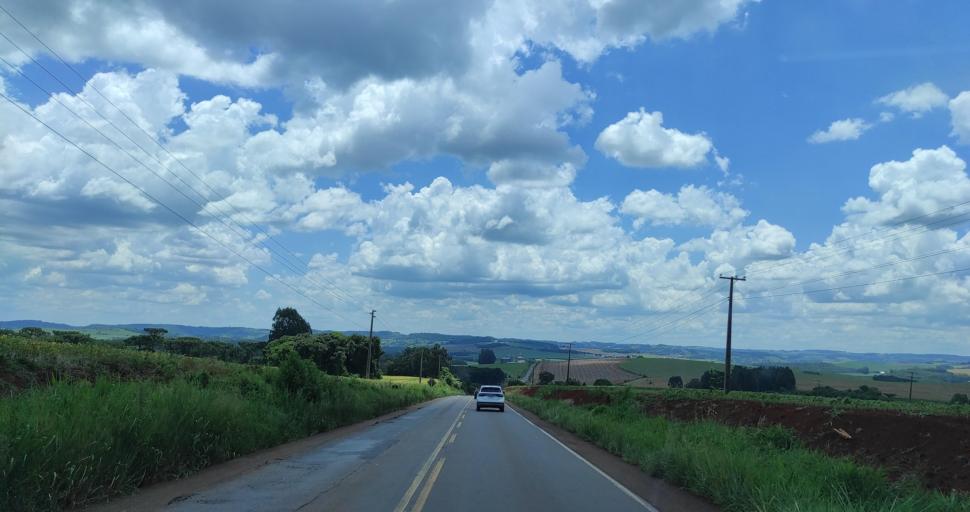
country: BR
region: Santa Catarina
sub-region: Xanxere
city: Xanxere
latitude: -26.7793
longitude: -52.4070
